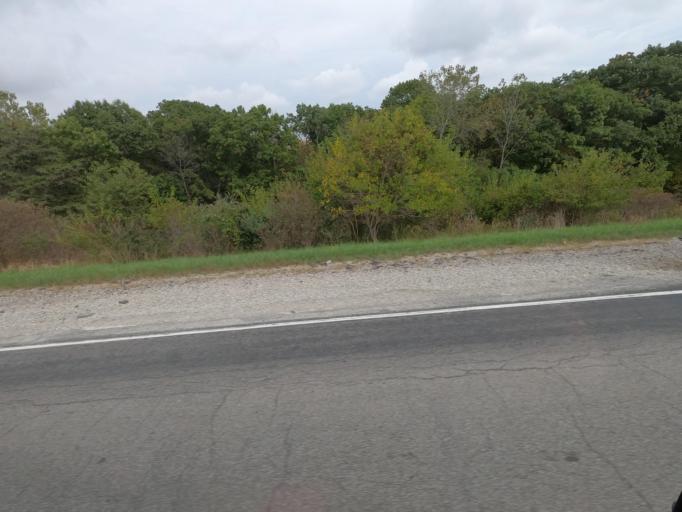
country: US
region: Iowa
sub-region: Wapello County
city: Ottumwa
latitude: 40.9317
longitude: -92.2282
